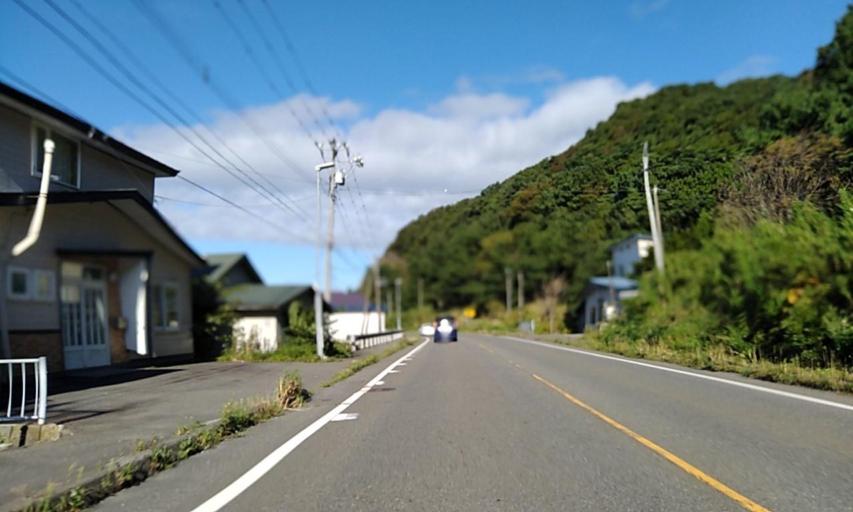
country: JP
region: Hokkaido
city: Shizunai-furukawacho
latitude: 42.2741
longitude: 142.4794
